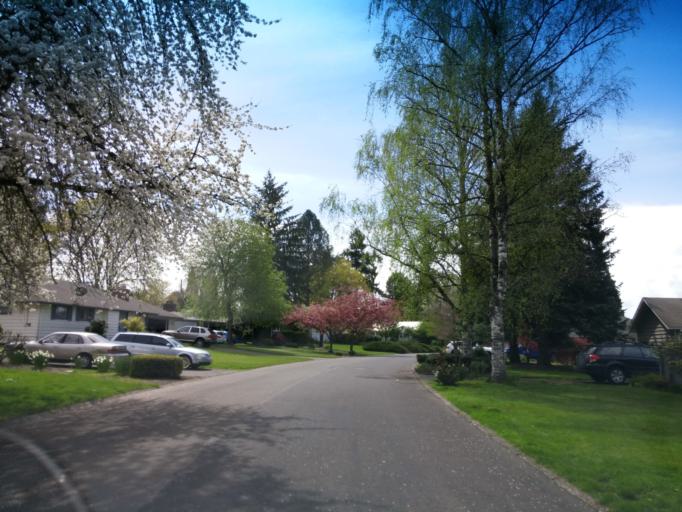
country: US
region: Oregon
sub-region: Washington County
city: Cedar Hills
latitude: 45.5064
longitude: -122.7982
